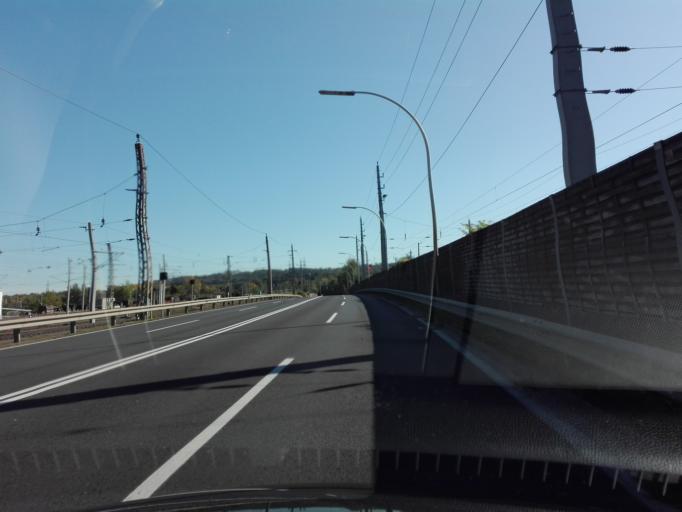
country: AT
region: Upper Austria
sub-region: Politischer Bezirk Urfahr-Umgebung
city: Steyregg
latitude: 48.2611
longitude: 14.3256
